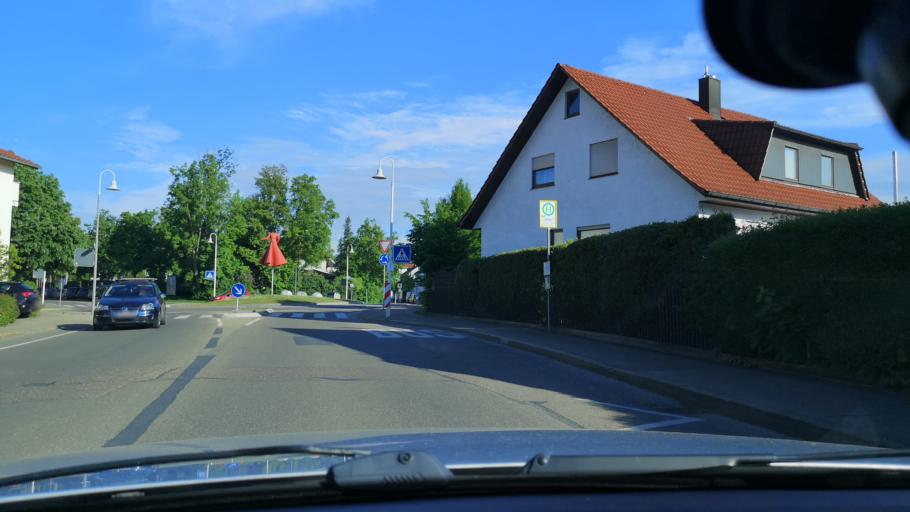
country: DE
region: Baden-Wuerttemberg
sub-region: Regierungsbezirk Stuttgart
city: Eislingen
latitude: 48.6993
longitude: 9.7031
